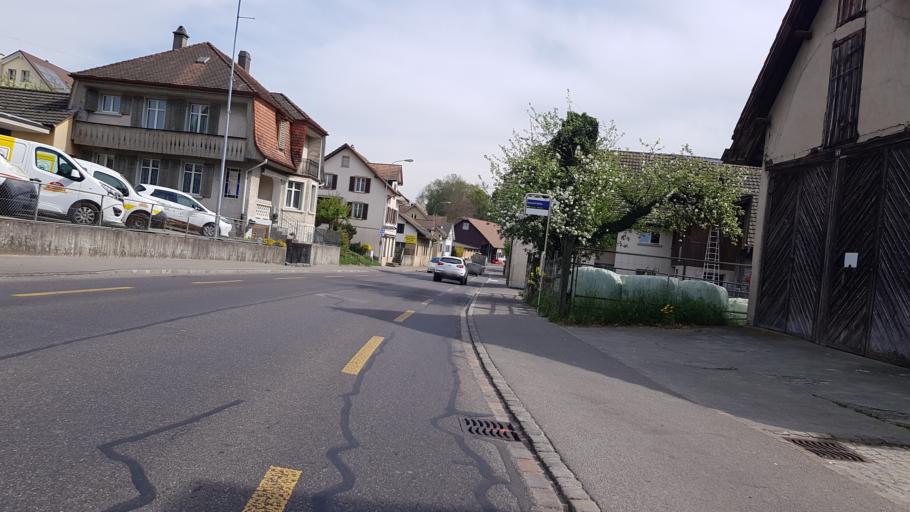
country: CH
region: Aargau
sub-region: Bezirk Kulm
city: Gontenschwil
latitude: 47.2850
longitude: 8.1519
